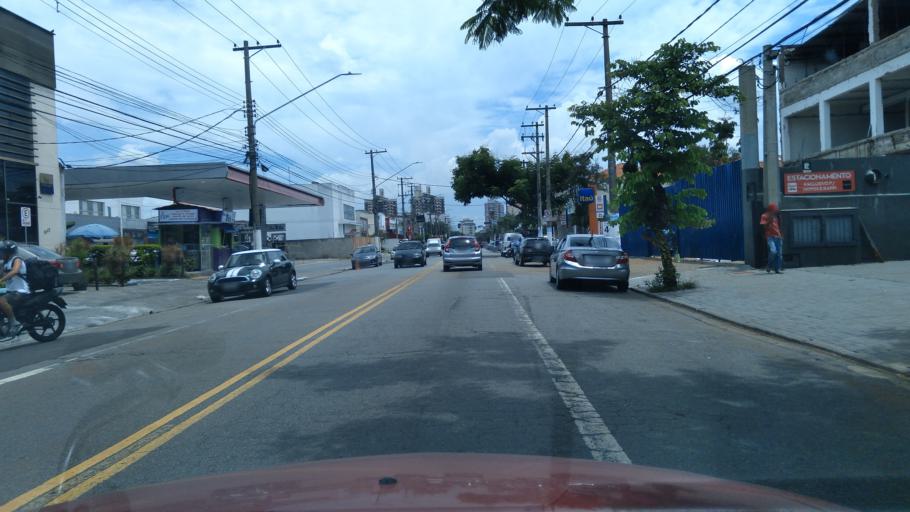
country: BR
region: Sao Paulo
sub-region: Sao Caetano Do Sul
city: Sao Caetano do Sul
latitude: -23.6151
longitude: -46.6174
